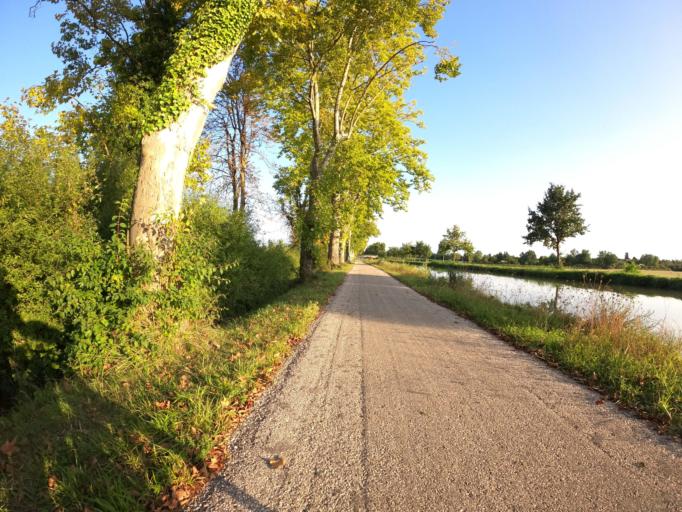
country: FR
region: Midi-Pyrenees
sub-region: Departement du Tarn-et-Garonne
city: Saint-Porquier
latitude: 44.0175
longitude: 1.1704
